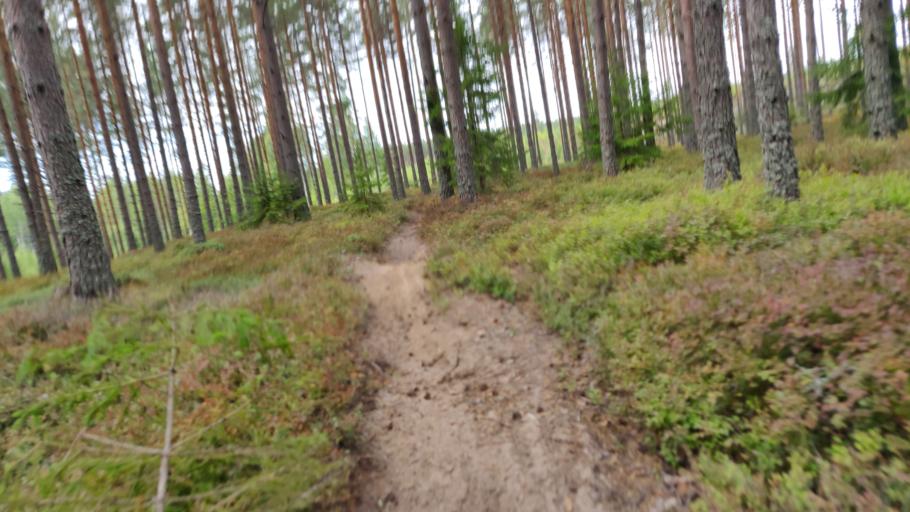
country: SE
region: Vaermland
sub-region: Hagfors Kommun
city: Hagfors
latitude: 60.0333
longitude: 13.5465
